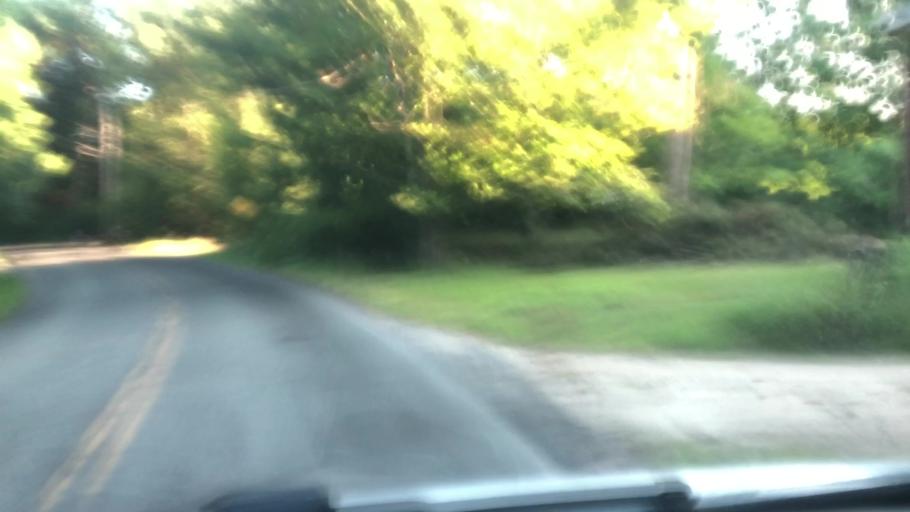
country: US
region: Massachusetts
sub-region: Hampshire County
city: Easthampton
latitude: 42.2870
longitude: -72.7141
